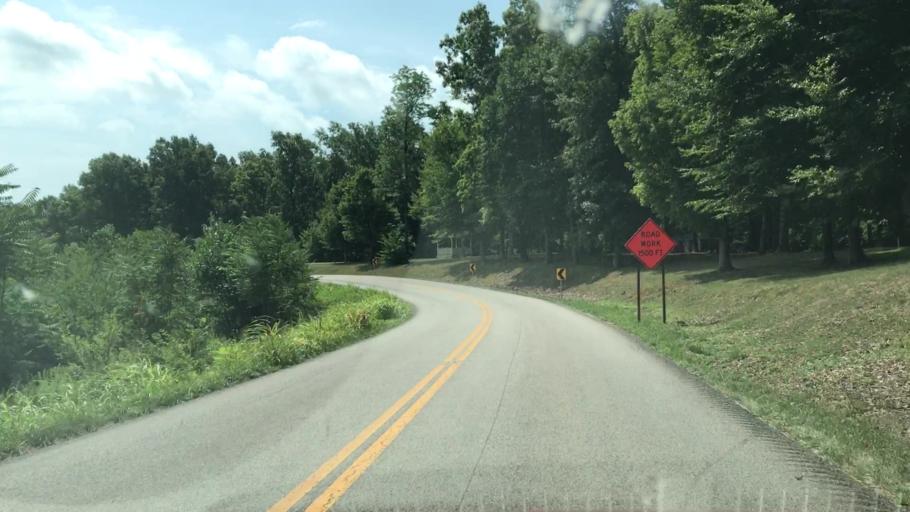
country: US
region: Kentucky
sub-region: Barren County
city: Glasgow
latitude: 36.9001
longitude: -85.8630
